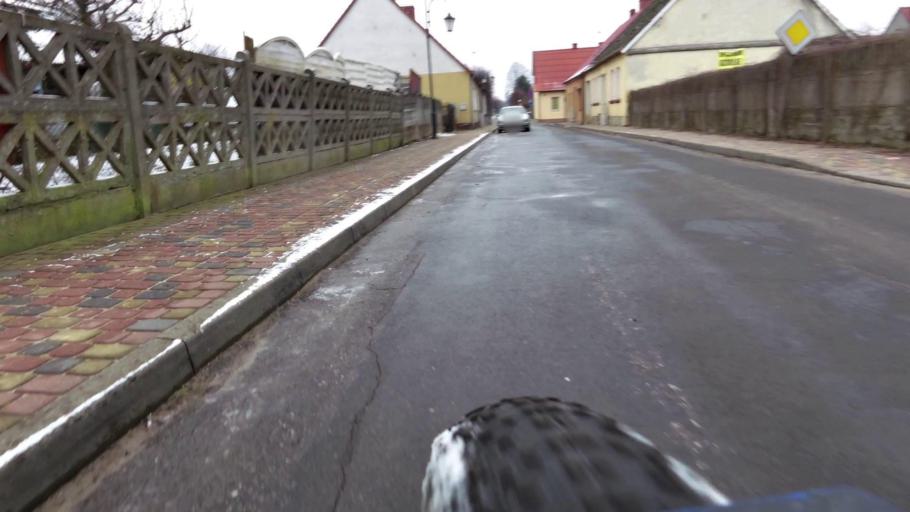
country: PL
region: West Pomeranian Voivodeship
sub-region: Powiat walecki
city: Miroslawiec
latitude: 53.3404
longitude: 16.0933
